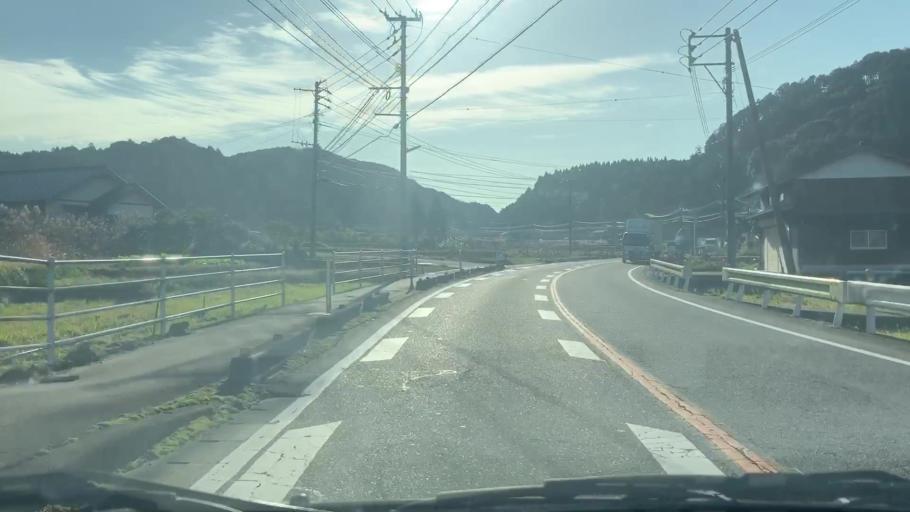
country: JP
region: Saga Prefecture
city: Takeocho-takeo
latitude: 33.2449
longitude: 130.0062
